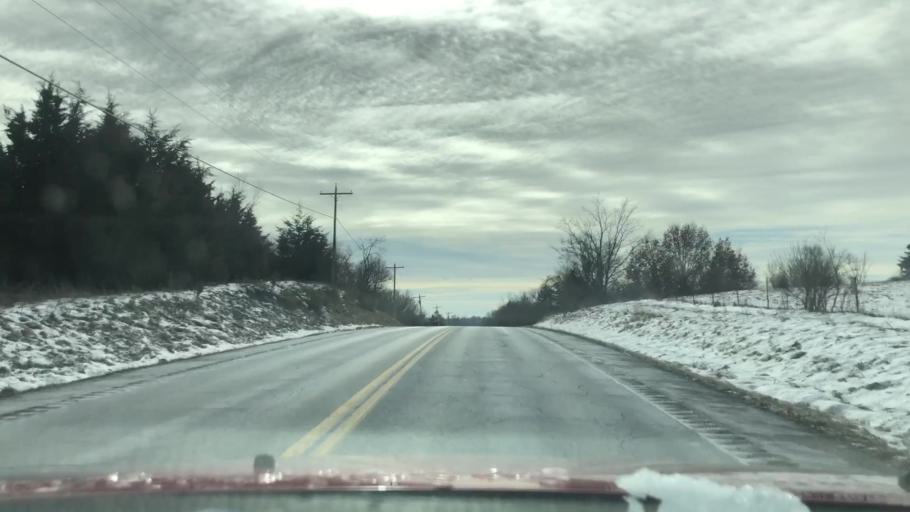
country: US
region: Missouri
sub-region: Jackson County
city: Oak Grove
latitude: 38.9648
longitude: -94.1311
